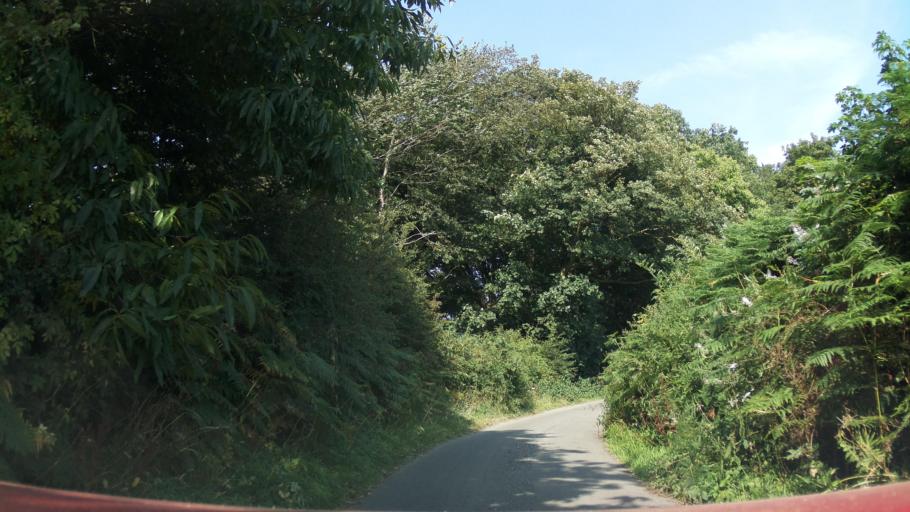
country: GB
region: England
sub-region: Derbyshire
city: Duffield
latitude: 52.9683
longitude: -1.5164
